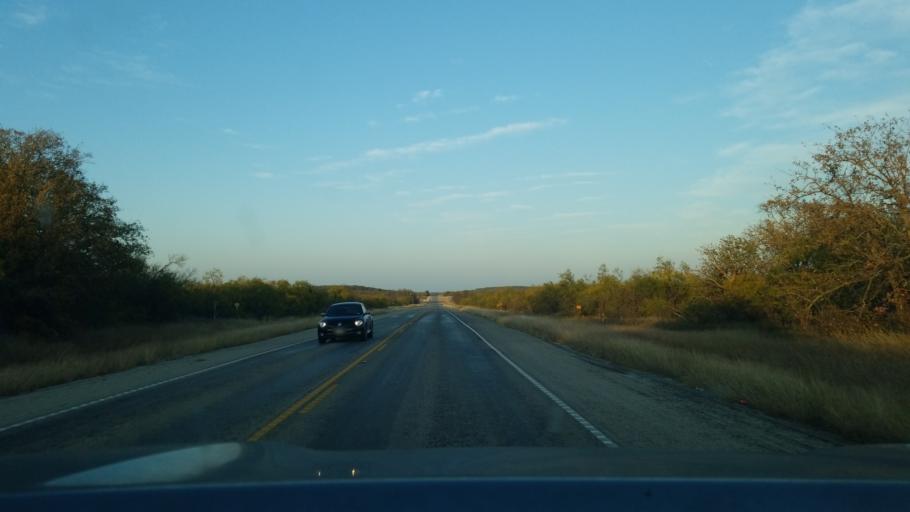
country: US
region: Texas
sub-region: Eastland County
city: Cisco
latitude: 32.4310
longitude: -98.9265
